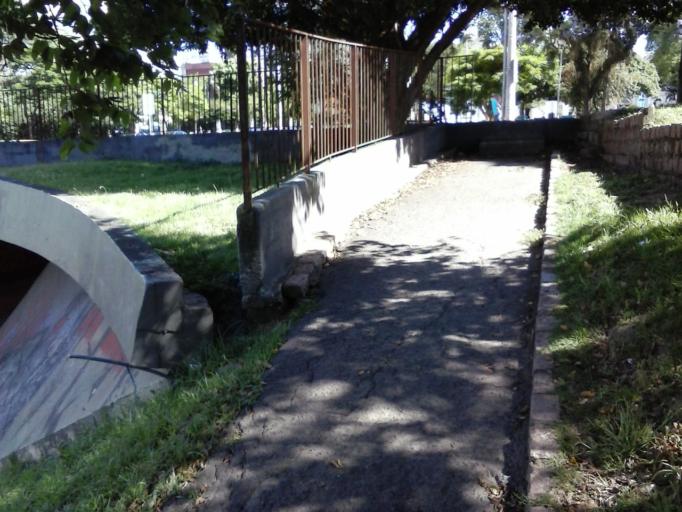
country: BR
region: Rio Grande do Sul
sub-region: Porto Alegre
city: Porto Alegre
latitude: -30.0307
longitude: -51.2191
